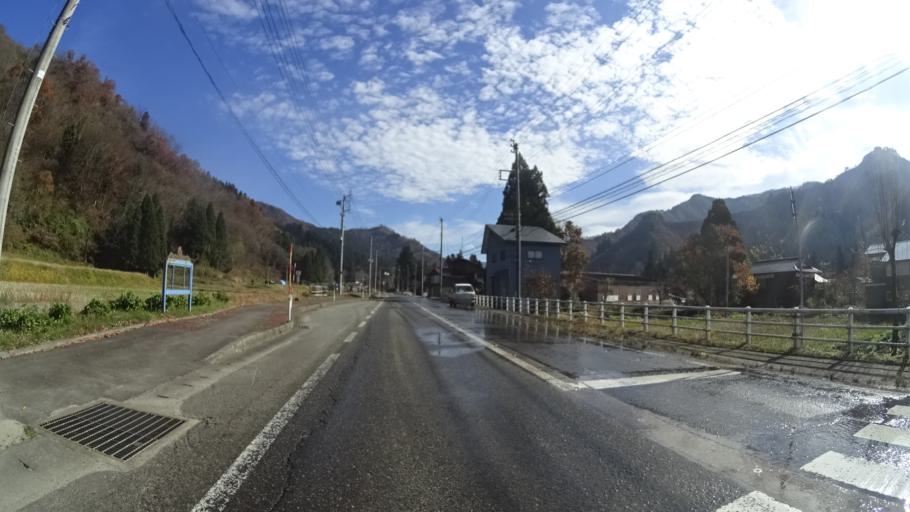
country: JP
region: Niigata
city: Muikamachi
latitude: 37.2250
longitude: 139.0149
